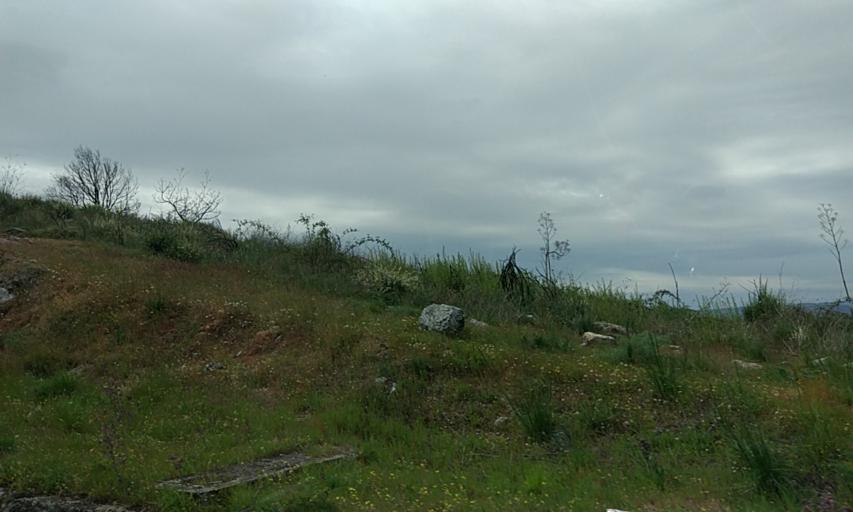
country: PT
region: Guarda
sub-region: Guarda
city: Guarda
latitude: 40.6146
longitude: -7.2827
